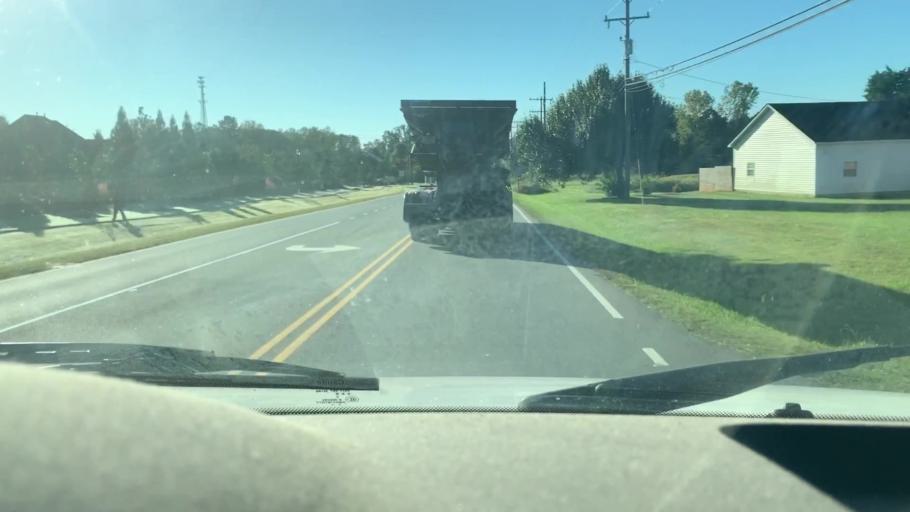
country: US
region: North Carolina
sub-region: Mecklenburg County
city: Huntersville
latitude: 35.4257
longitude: -80.7560
